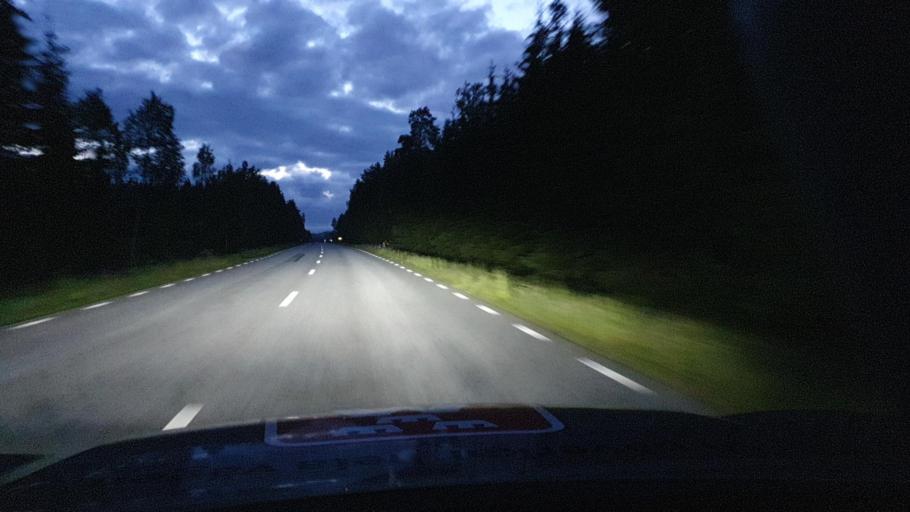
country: SE
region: OErebro
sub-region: Karlskoga Kommun
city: Karlskoga
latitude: 59.4163
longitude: 14.5170
